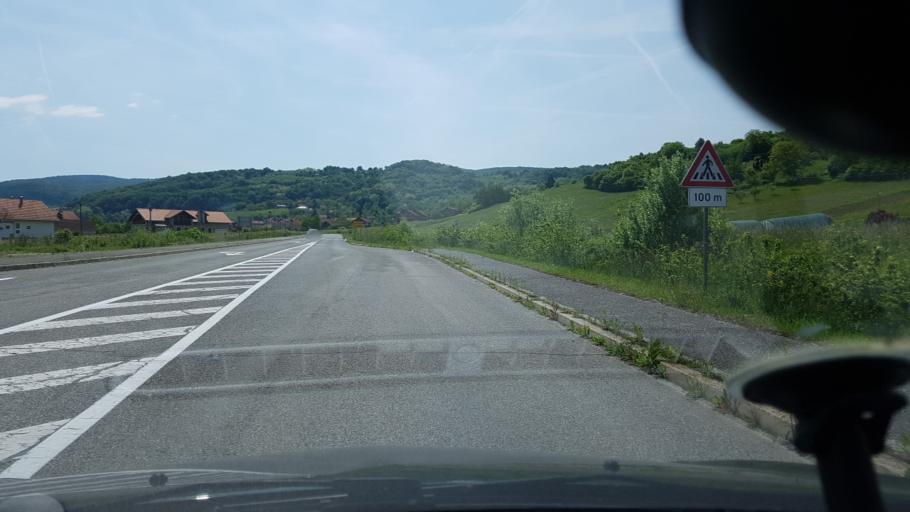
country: HR
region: Krapinsko-Zagorska
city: Marija Bistrica
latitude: 45.9999
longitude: 16.1163
